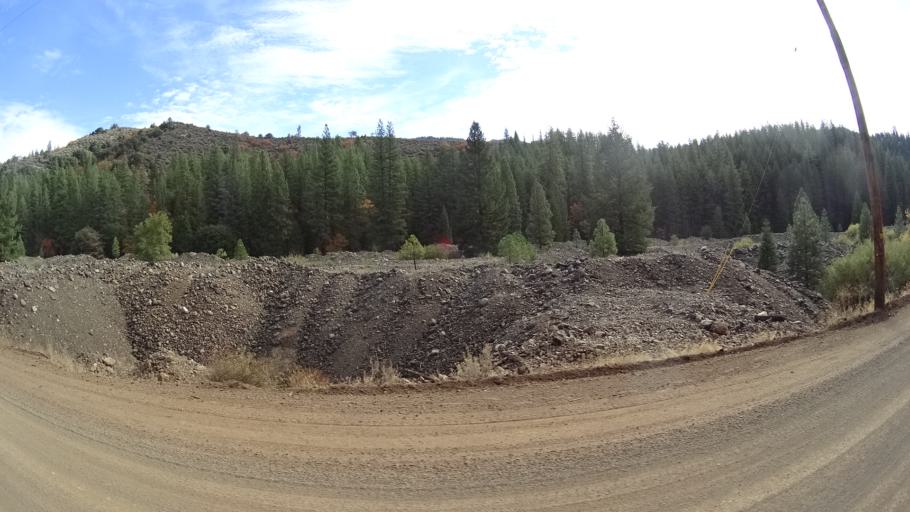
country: US
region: California
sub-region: Siskiyou County
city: Yreka
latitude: 41.6905
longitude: -122.8184
